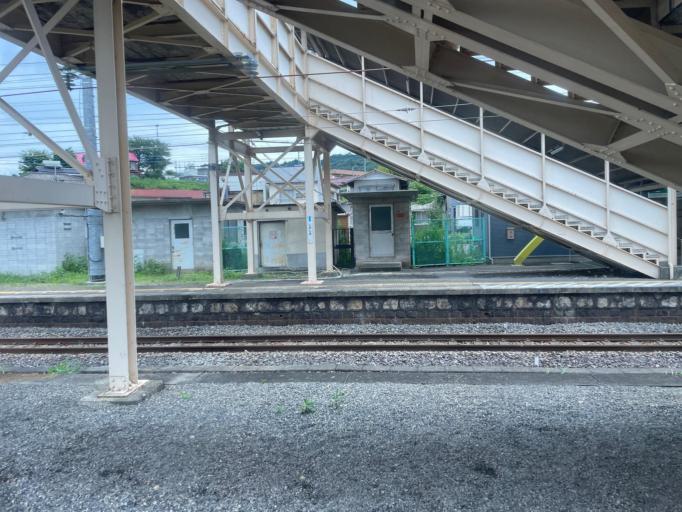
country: JP
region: Gunma
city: Shibukawa
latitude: 36.5386
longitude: 139.0337
